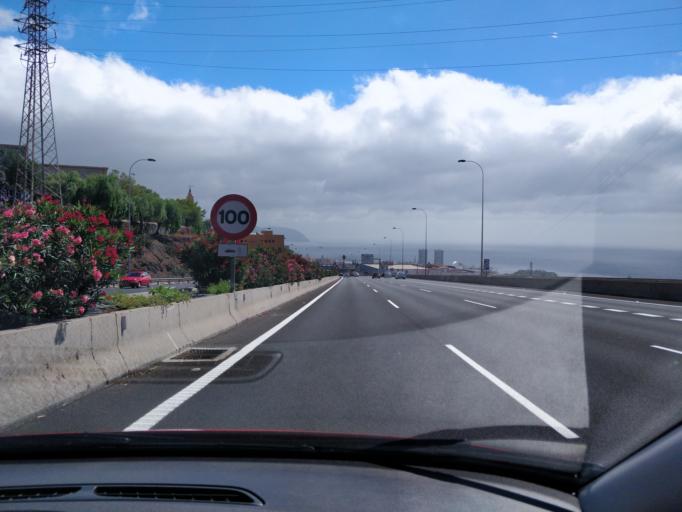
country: ES
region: Canary Islands
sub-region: Provincia de Santa Cruz de Tenerife
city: Santa Cruz de Tenerife
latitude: 28.4485
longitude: -16.2818
